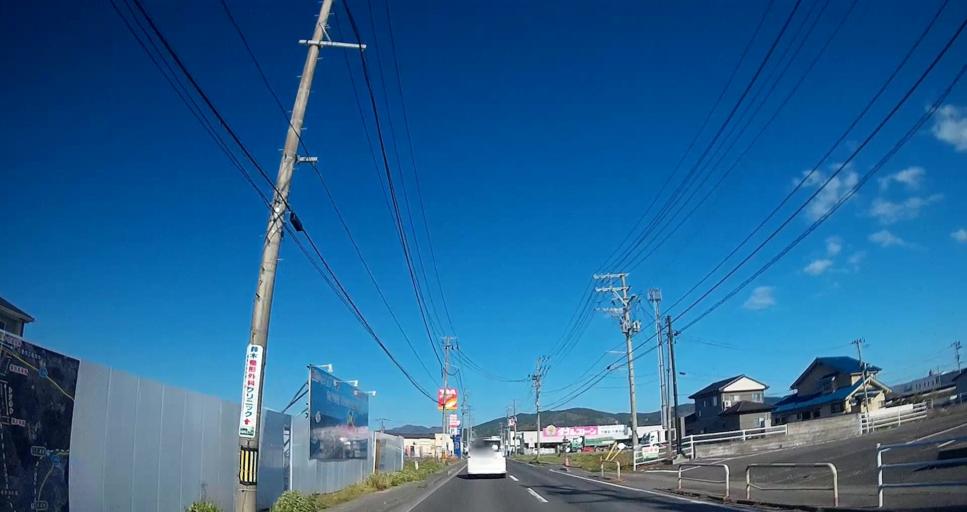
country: JP
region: Miyagi
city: Ishinomaki
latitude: 38.4179
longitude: 141.3426
